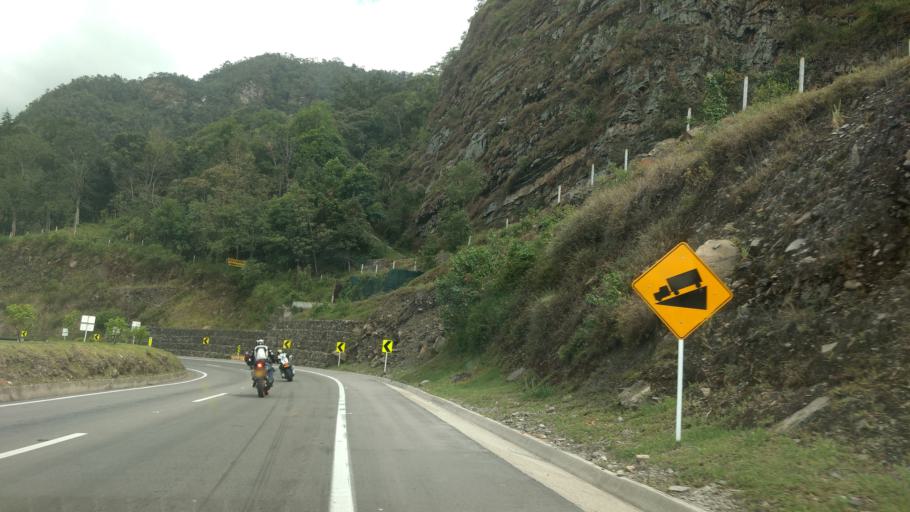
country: CO
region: Cundinamarca
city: San Francisco
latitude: 4.9450
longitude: -74.2932
